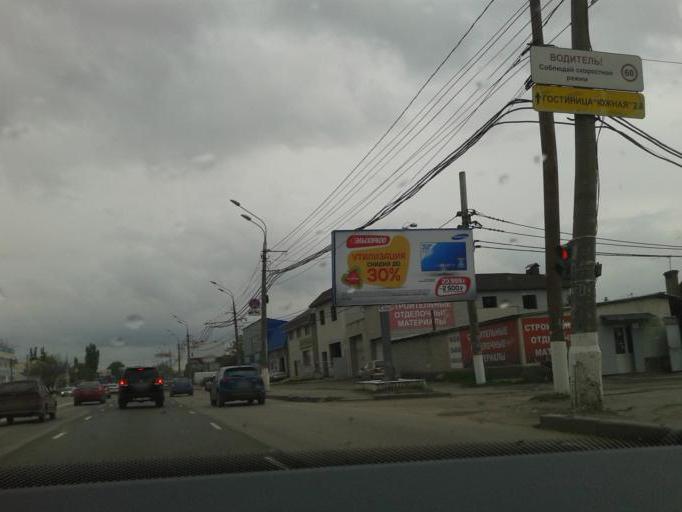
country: RU
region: Volgograd
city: Volgograd
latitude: 48.6931
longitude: 44.4636
